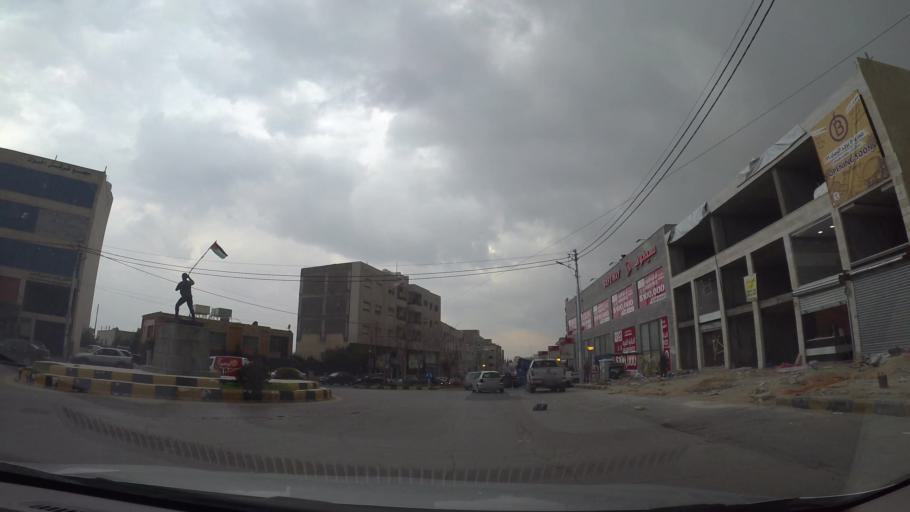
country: JO
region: Amman
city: Umm as Summaq
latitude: 31.8874
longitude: 35.8571
